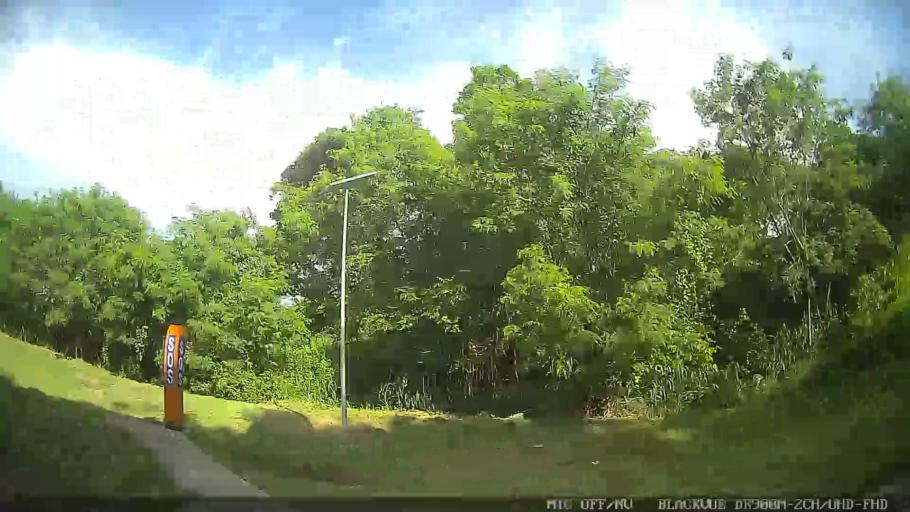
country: BR
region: Sao Paulo
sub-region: Tiete
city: Tiete
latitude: -23.1013
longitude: -47.6916
